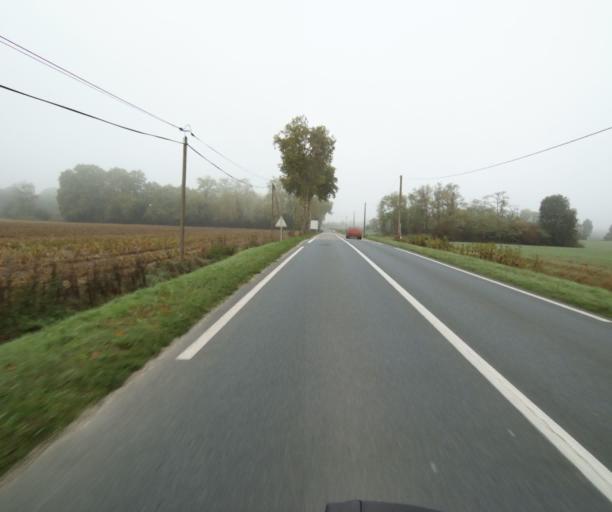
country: FR
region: Midi-Pyrenees
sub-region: Departement du Tarn-et-Garonne
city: Saint-Nauphary
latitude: 43.9448
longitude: 1.4620
